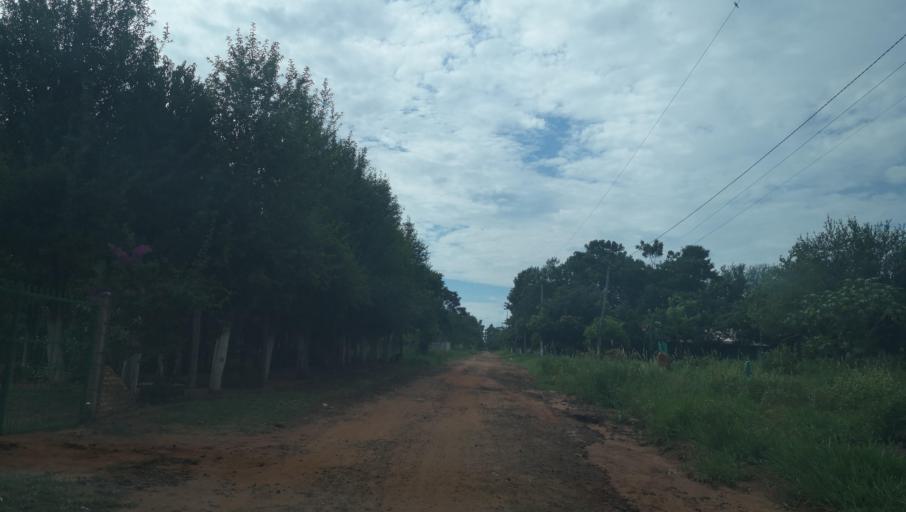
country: PY
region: San Pedro
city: Capiibary
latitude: -24.7197
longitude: -56.0219
